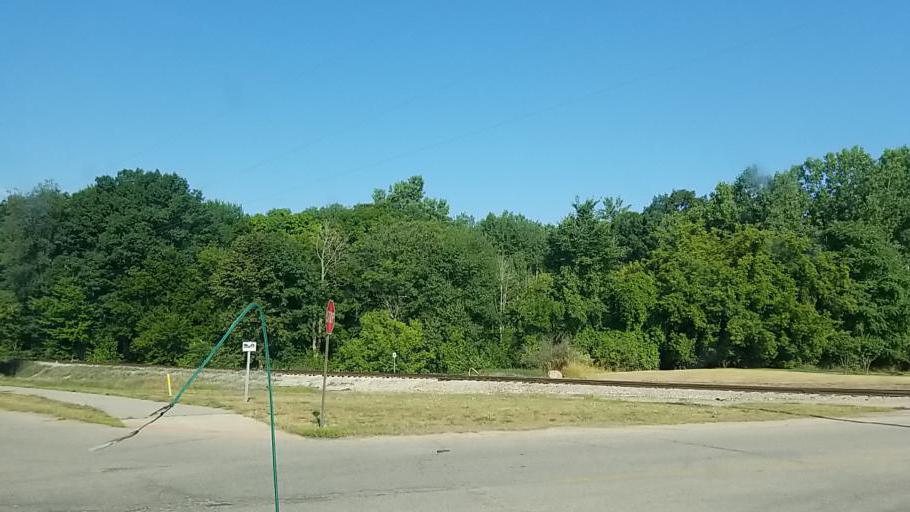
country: US
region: Michigan
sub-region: Newaygo County
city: Fremont
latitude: 43.4647
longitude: -85.9597
